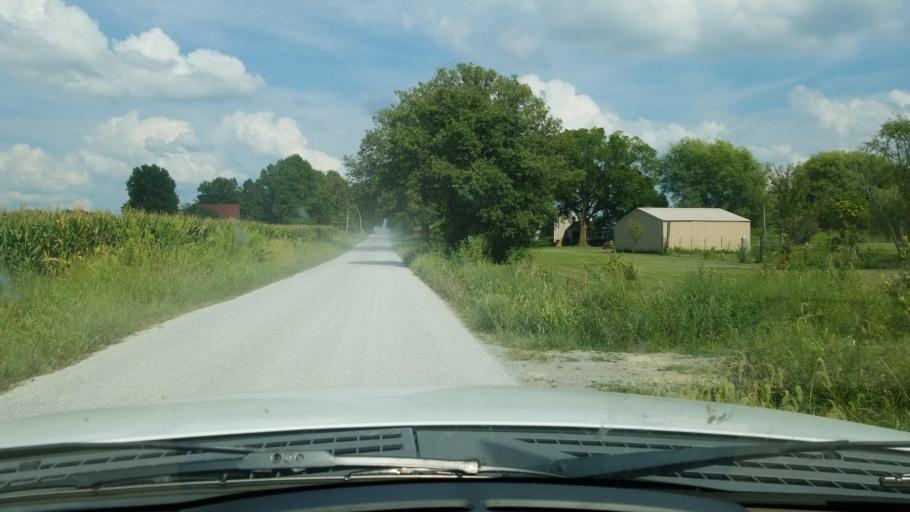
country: US
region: Illinois
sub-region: Saline County
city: Eldorado
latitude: 37.8344
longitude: -88.4402
